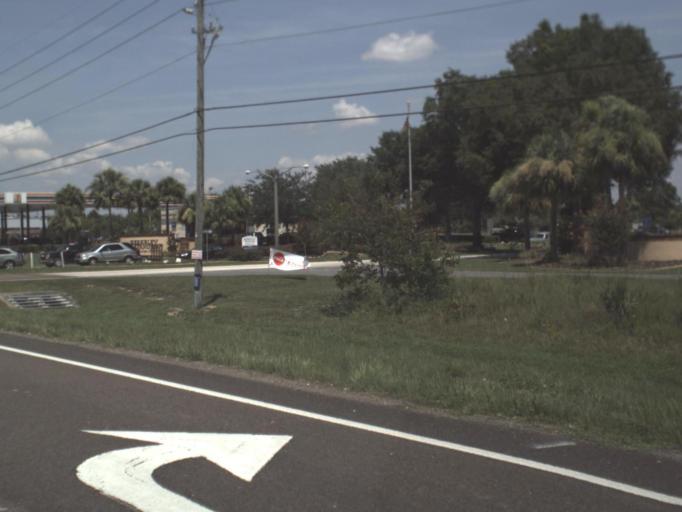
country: US
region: Florida
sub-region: Hernando County
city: Timber Pines
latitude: 28.4962
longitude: -82.5947
